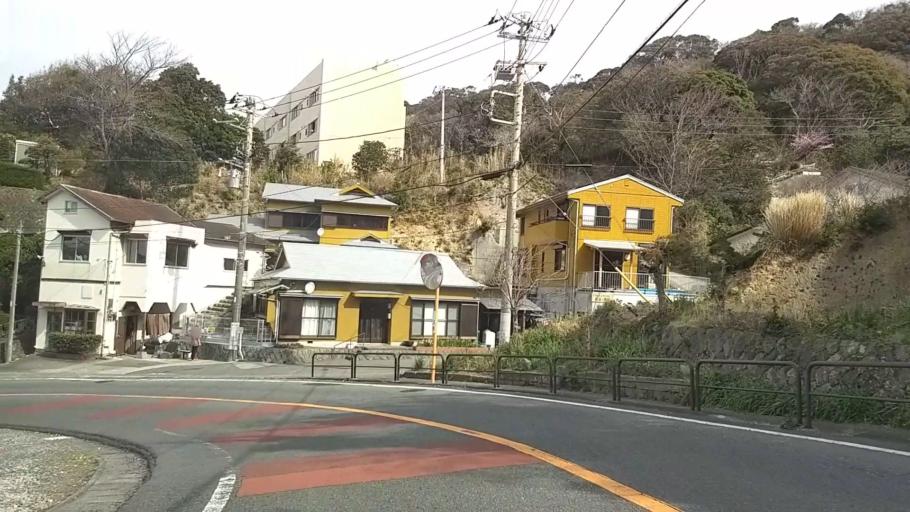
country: JP
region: Shizuoka
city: Shimoda
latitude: 34.6701
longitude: 138.9651
